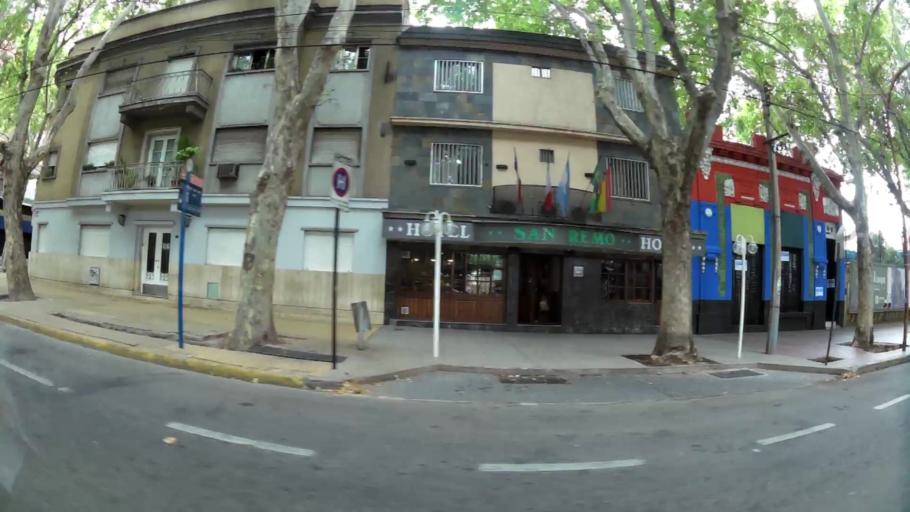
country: AR
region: Mendoza
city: Mendoza
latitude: -32.8830
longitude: -68.8436
